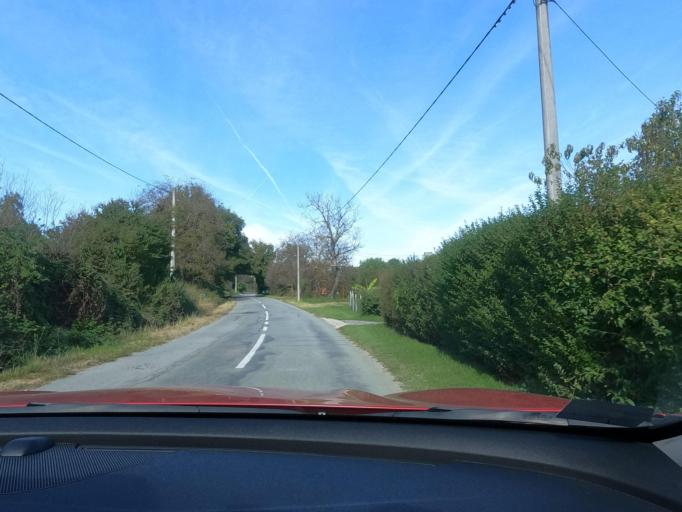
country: HR
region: Sisacko-Moslavacka
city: Petrinja
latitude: 45.3958
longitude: 16.2922
